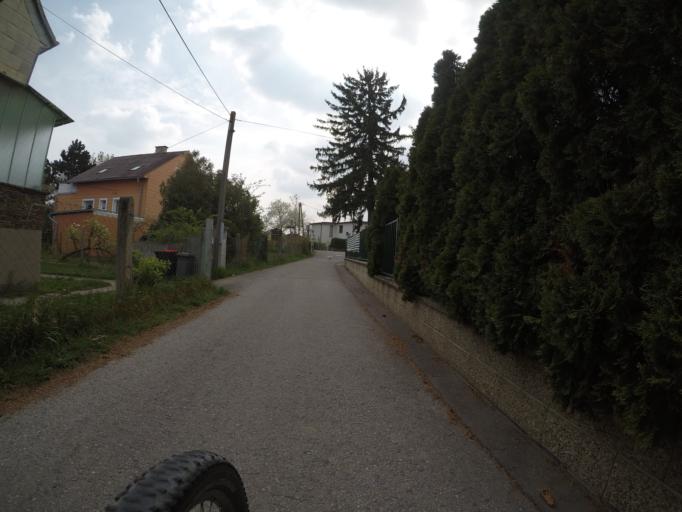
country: AT
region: Lower Austria
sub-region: Politischer Bezirk Baden
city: Pfaffstatten
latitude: 48.0005
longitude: 16.2603
